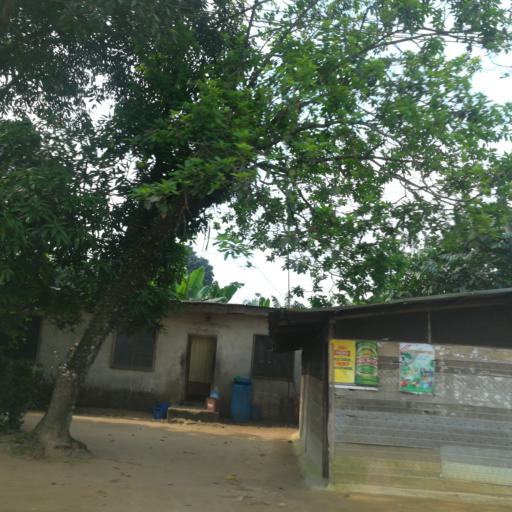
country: NG
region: Rivers
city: Okrika
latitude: 4.7813
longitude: 7.1455
